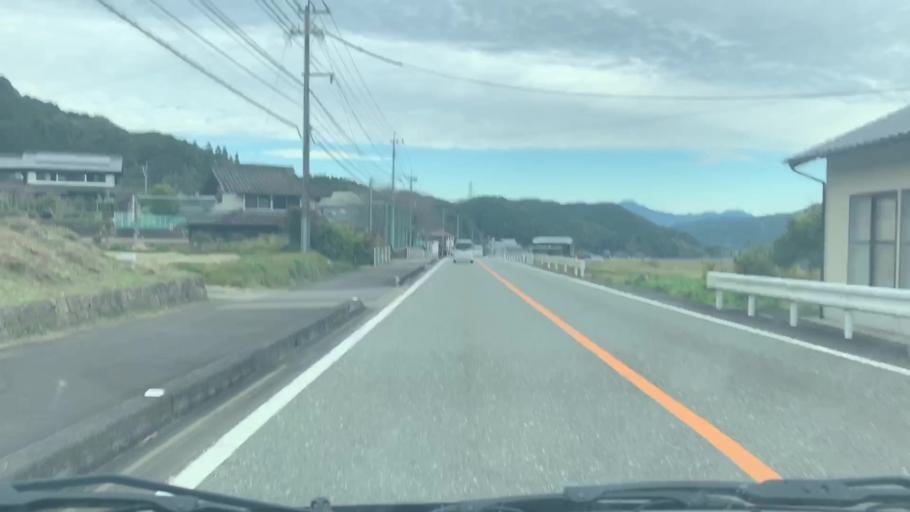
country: JP
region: Saga Prefecture
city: Takeocho-takeo
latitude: 33.1724
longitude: 129.9696
